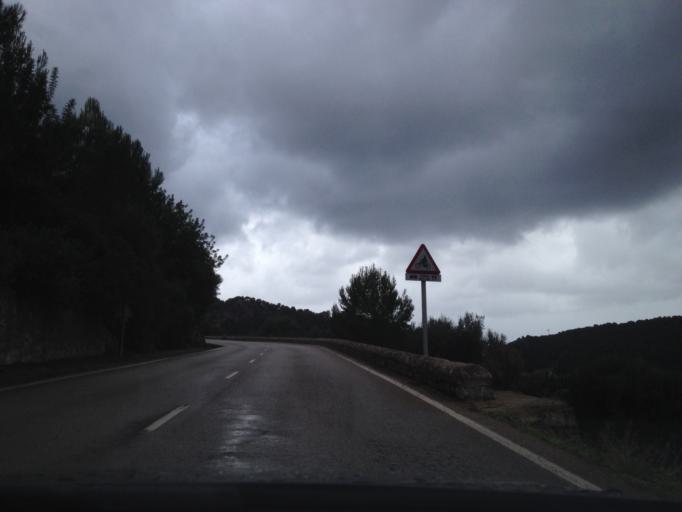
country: ES
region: Balearic Islands
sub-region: Illes Balears
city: Soller
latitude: 39.7725
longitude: 2.7018
